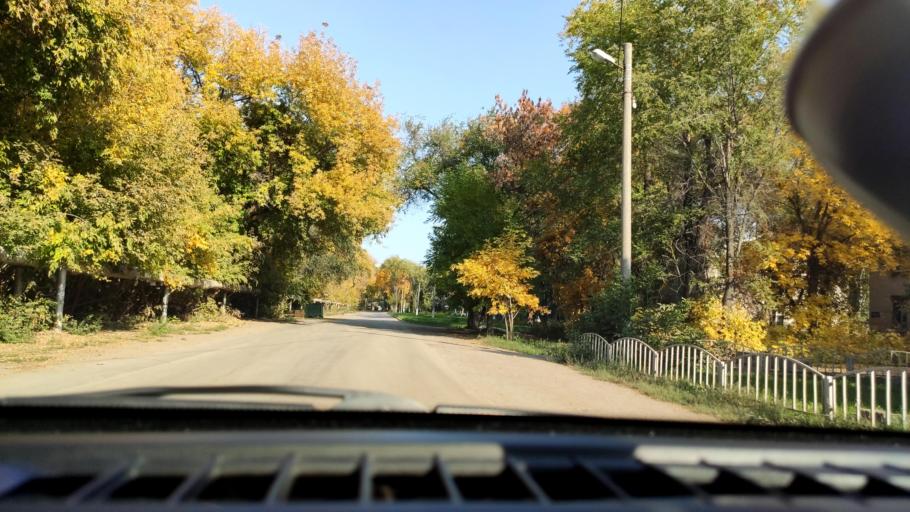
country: RU
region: Samara
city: Smyshlyayevka
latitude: 53.1890
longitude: 50.2880
